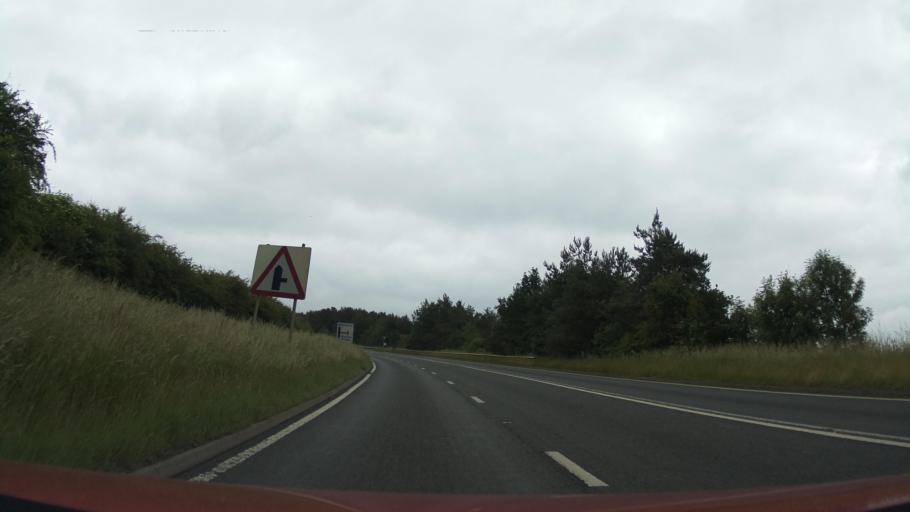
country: GB
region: England
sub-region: District of Rutland
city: Ridlington
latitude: 52.5945
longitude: -0.7798
